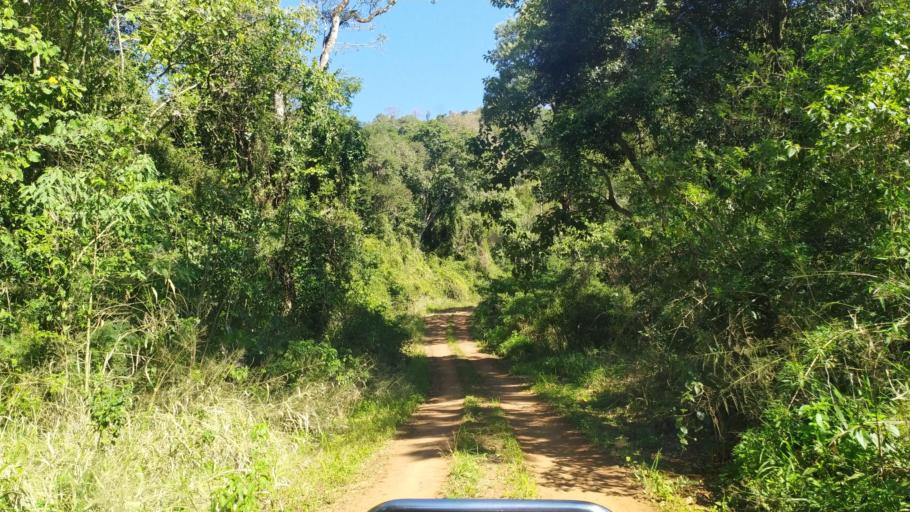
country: AR
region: Misiones
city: El Alcazar
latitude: -26.7602
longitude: -54.5832
